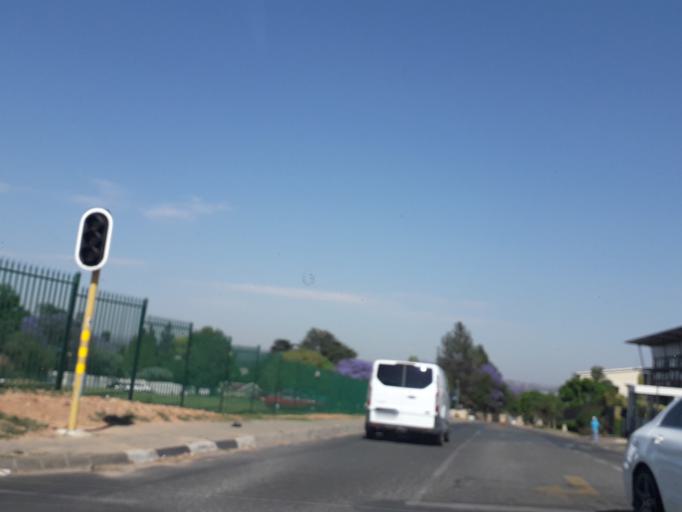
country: ZA
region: Gauteng
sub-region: City of Johannesburg Metropolitan Municipality
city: Midrand
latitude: -26.0638
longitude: 28.0243
